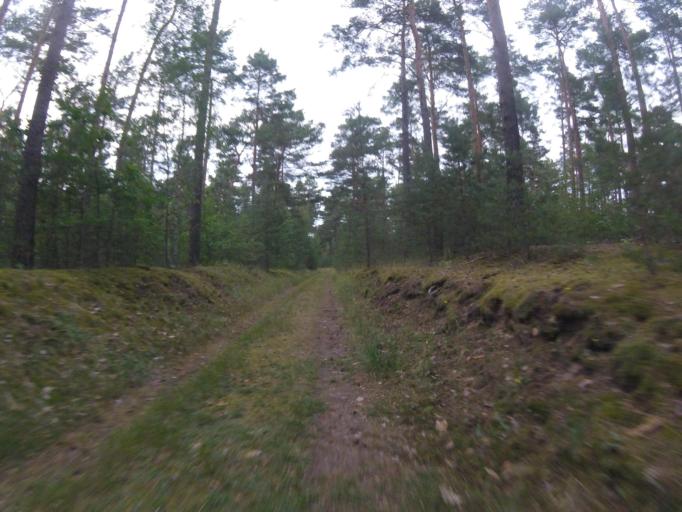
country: DE
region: Brandenburg
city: Gross Koris
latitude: 52.1584
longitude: 13.6807
